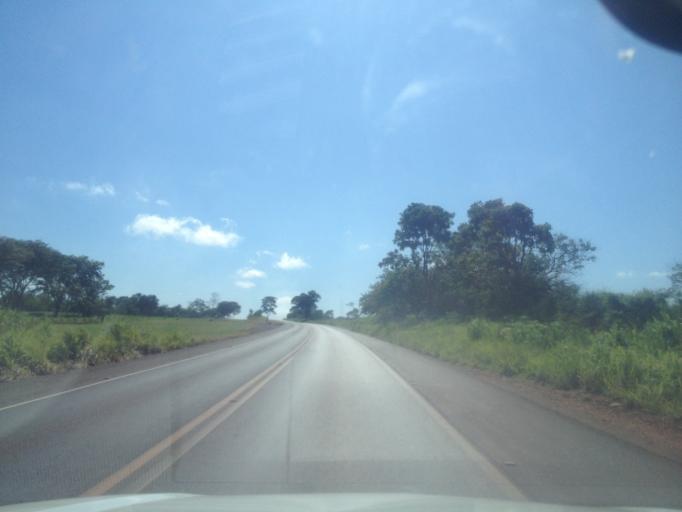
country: BR
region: Minas Gerais
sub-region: Santa Vitoria
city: Santa Vitoria
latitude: -19.0476
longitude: -50.4870
